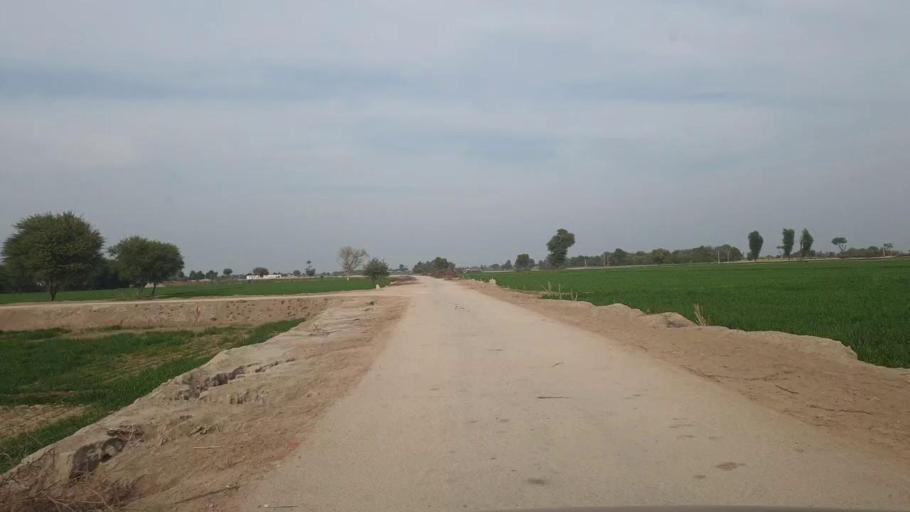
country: PK
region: Sindh
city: Shahpur Chakar
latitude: 26.1136
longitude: 68.5218
